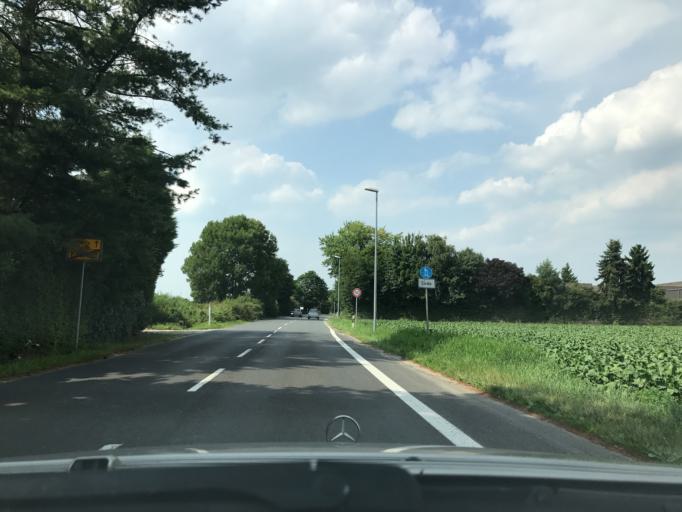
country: DE
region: North Rhine-Westphalia
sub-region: Regierungsbezirk Dusseldorf
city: Krefeld
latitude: 51.3898
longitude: 6.5995
